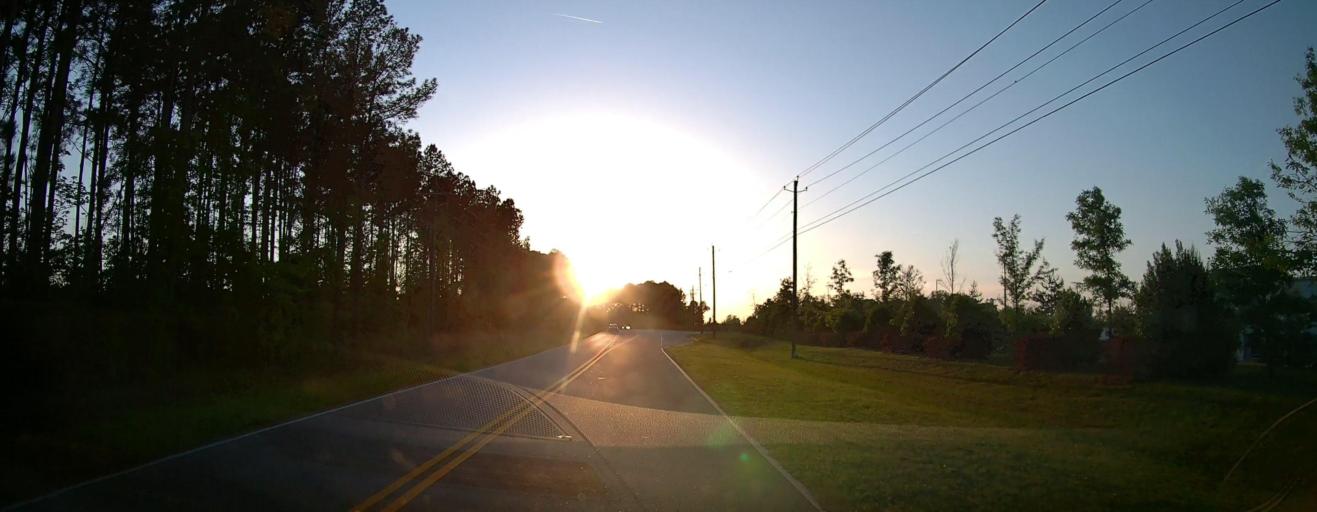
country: US
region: Georgia
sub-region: Henry County
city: McDonough
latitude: 33.4043
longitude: -84.1289
